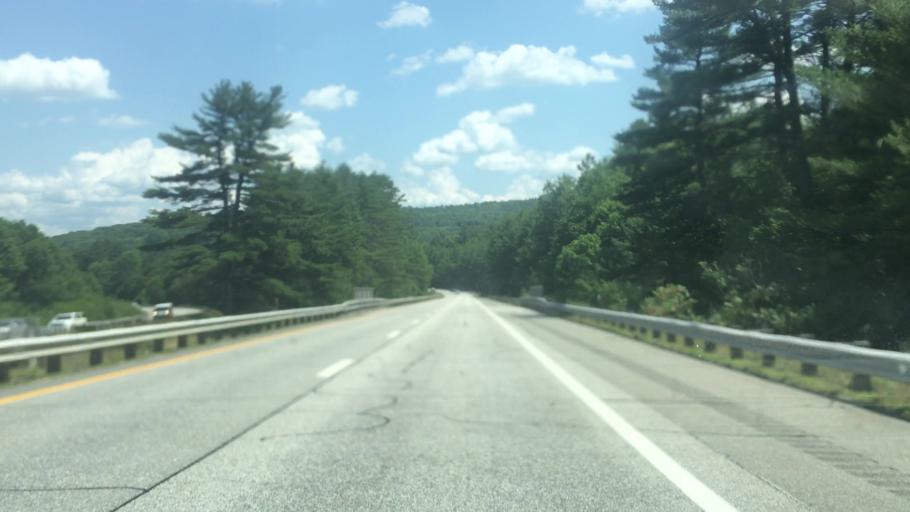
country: US
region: New Hampshire
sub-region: Merrimack County
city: Henniker
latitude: 43.2739
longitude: -71.8098
